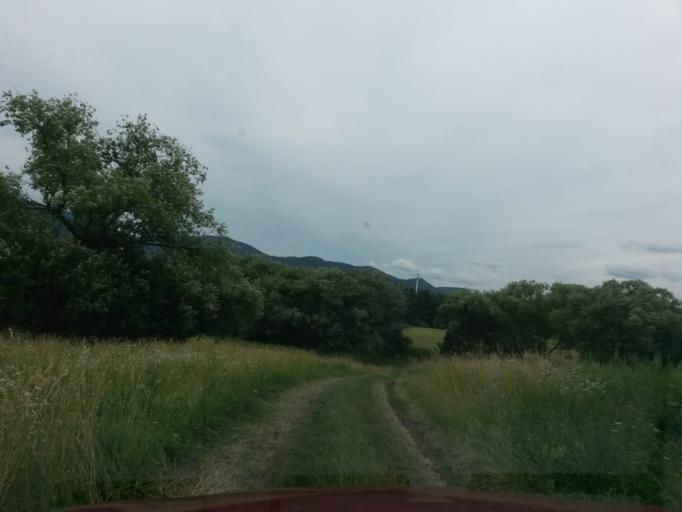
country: SK
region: Nitriansky
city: Handlova
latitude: 48.7411
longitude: 18.7512
